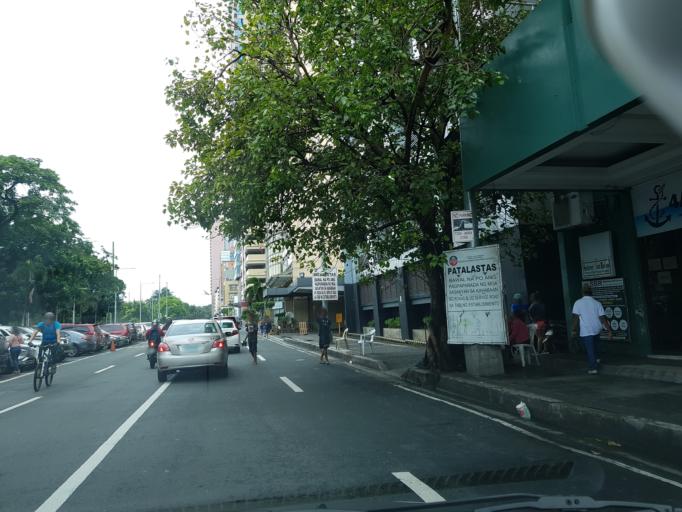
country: PH
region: Metro Manila
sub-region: City of Manila
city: Port Area
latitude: 14.5754
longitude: 120.9801
